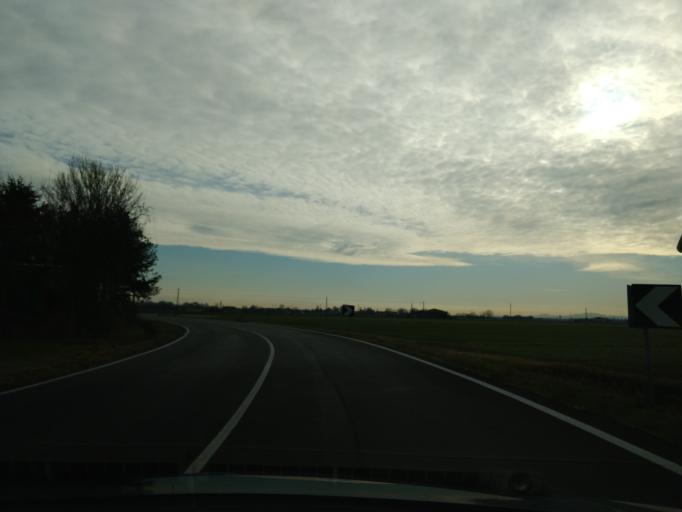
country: IT
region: Emilia-Romagna
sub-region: Provincia di Bologna
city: Argelato
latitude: 44.6476
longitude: 11.3217
